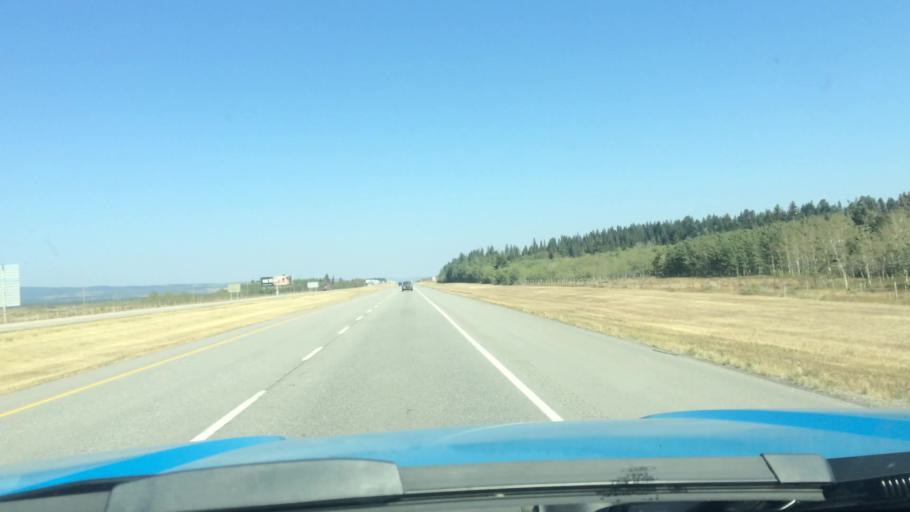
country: CA
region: Alberta
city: Canmore
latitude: 51.1089
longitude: -115.0070
